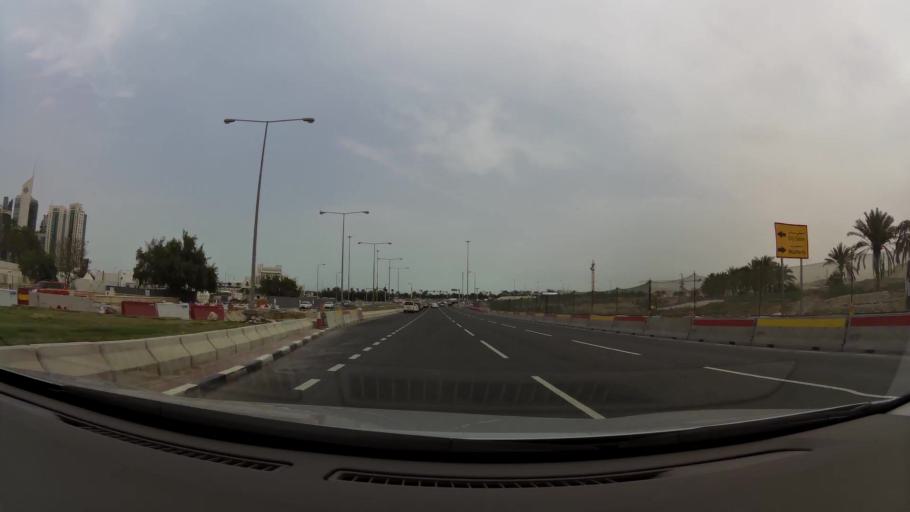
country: QA
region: Baladiyat ad Dawhah
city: Doha
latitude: 25.3107
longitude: 51.5126
